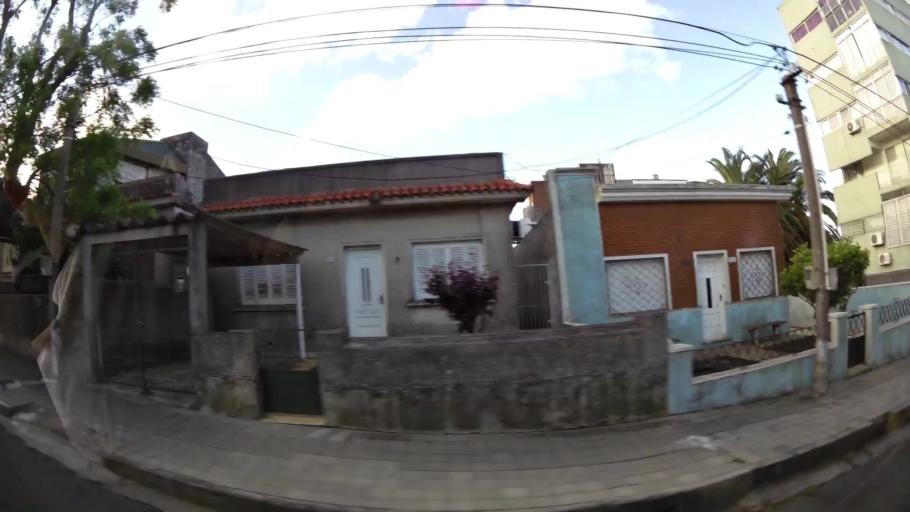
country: UY
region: Montevideo
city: Montevideo
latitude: -34.8882
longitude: -56.2536
